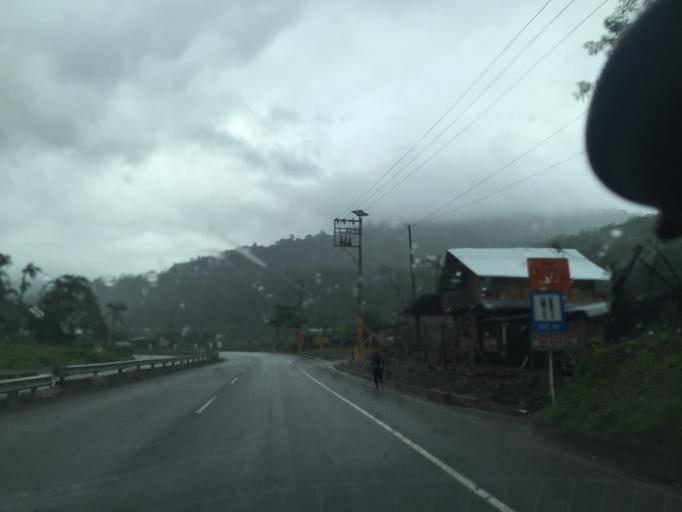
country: CO
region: Valle del Cauca
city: Buenaventura
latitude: 3.8661
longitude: -76.8267
